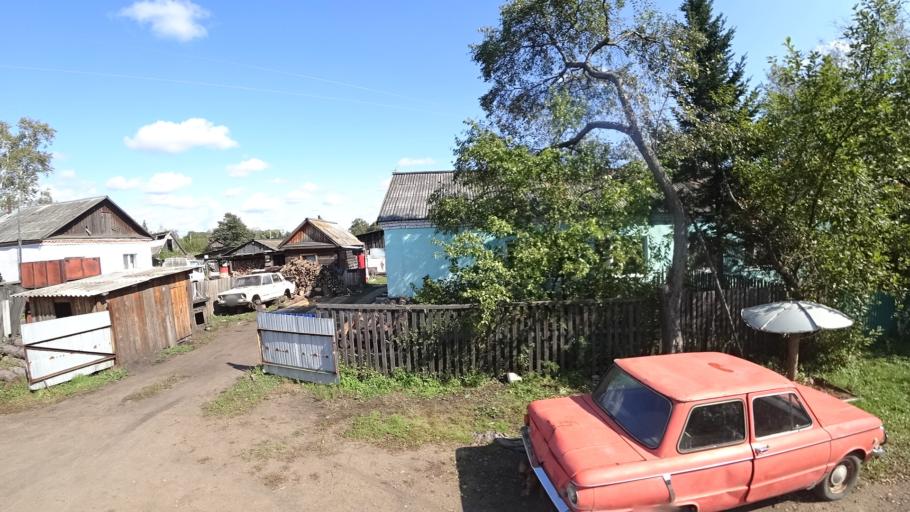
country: RU
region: Amur
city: Arkhara
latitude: 49.4000
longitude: 130.1478
